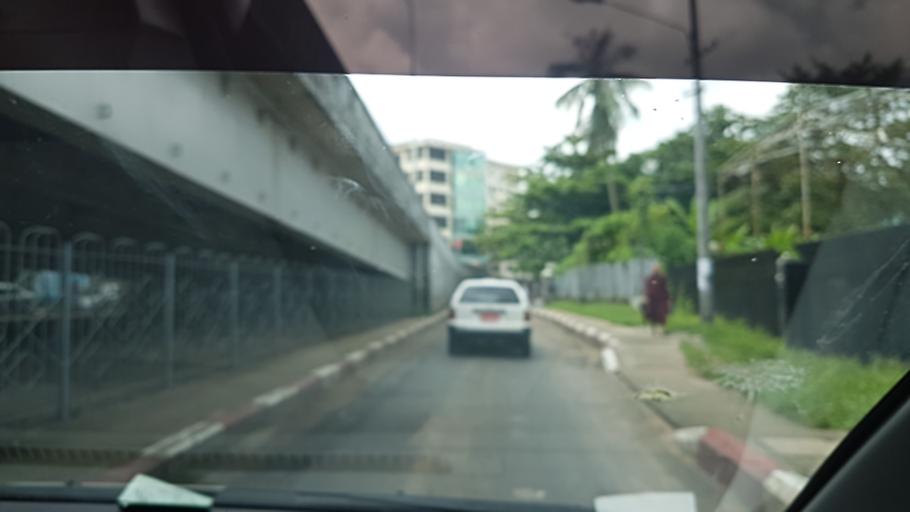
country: MM
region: Yangon
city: Yangon
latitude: 16.8046
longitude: 96.1560
